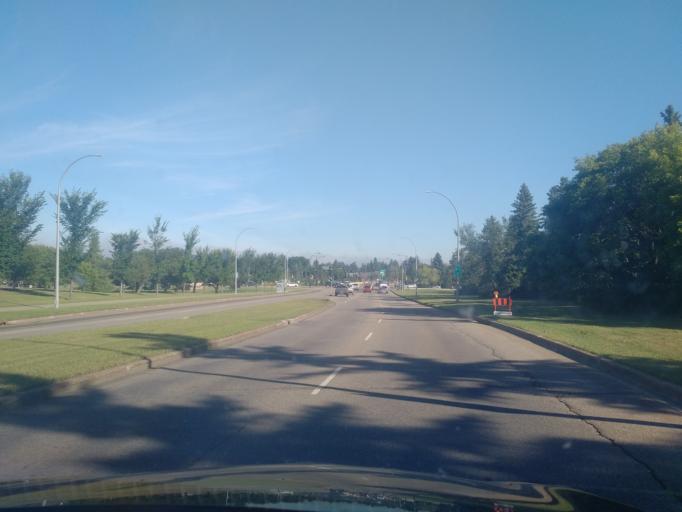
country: CA
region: Alberta
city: Edmonton
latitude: 53.5065
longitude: -113.5230
